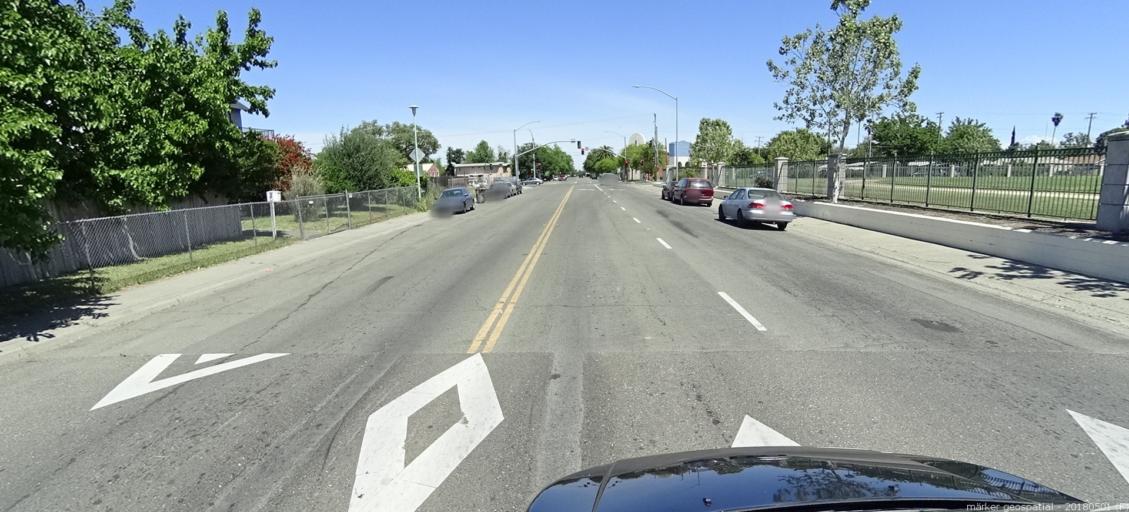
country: US
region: California
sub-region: Sacramento County
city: Rio Linda
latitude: 38.6356
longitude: -121.4385
